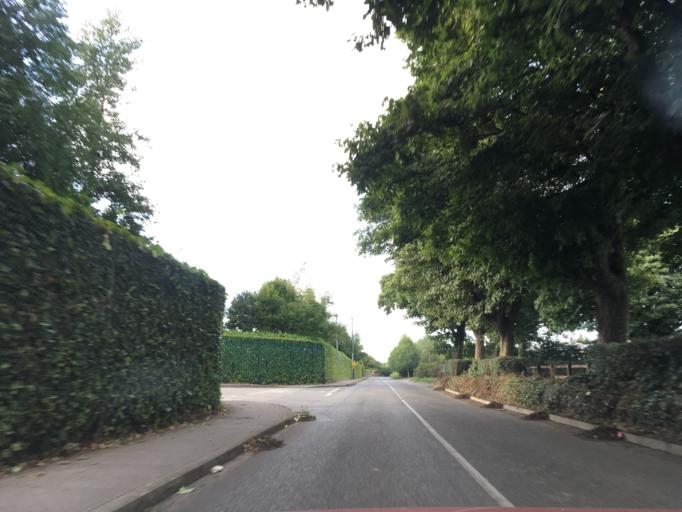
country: IE
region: Munster
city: Cashel
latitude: 52.5031
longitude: -7.8868
